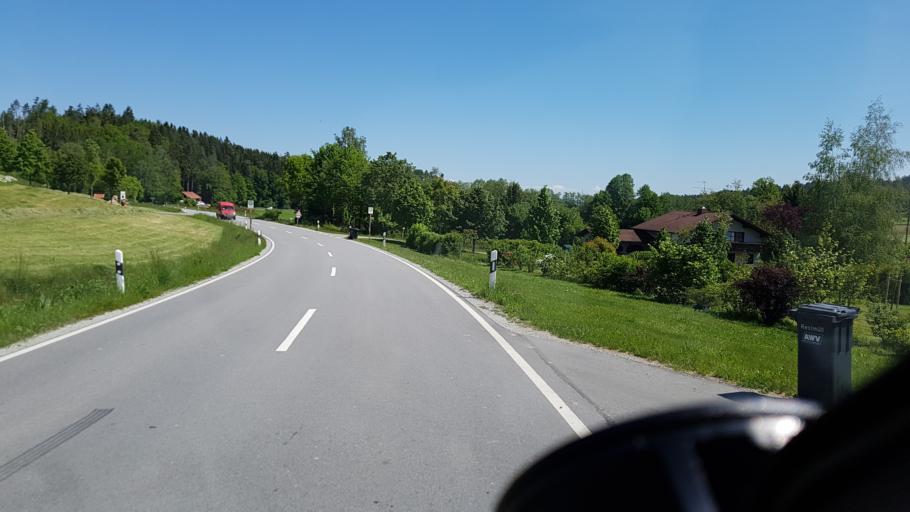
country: DE
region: Bavaria
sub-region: Lower Bavaria
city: Postmunster
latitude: 48.3847
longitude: 12.9119
